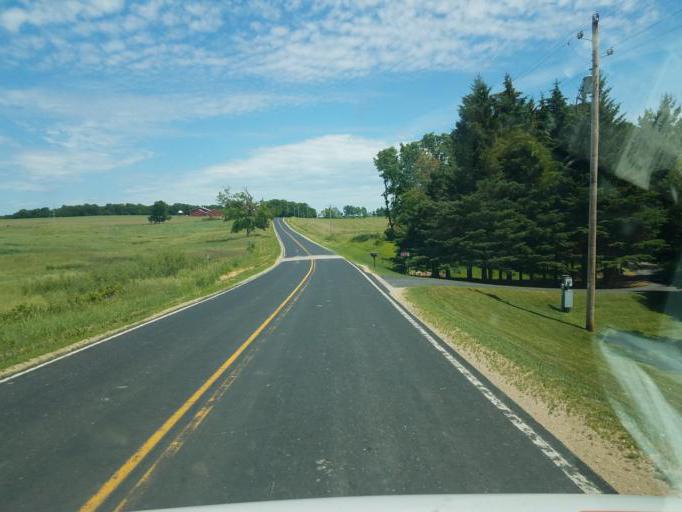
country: US
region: Wisconsin
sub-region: Vernon County
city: Hillsboro
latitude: 43.5940
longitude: -90.3211
